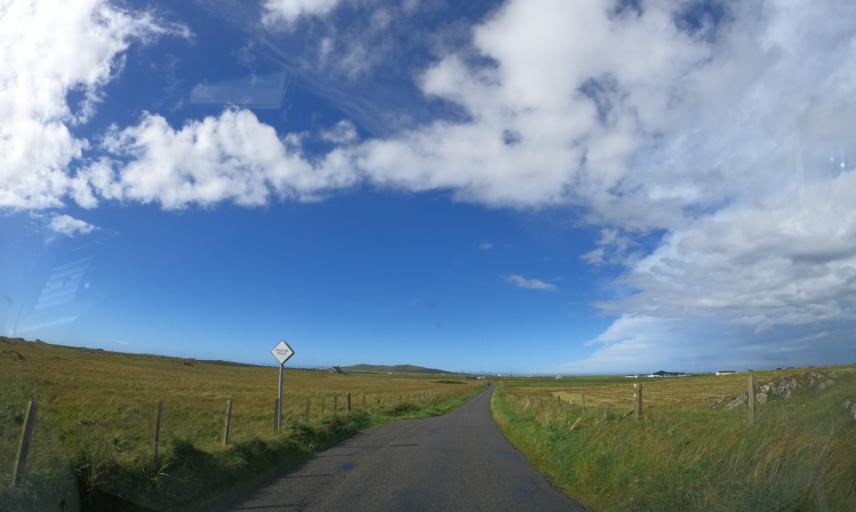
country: GB
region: Scotland
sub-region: Eilean Siar
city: Barra
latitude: 56.5208
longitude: -6.9066
